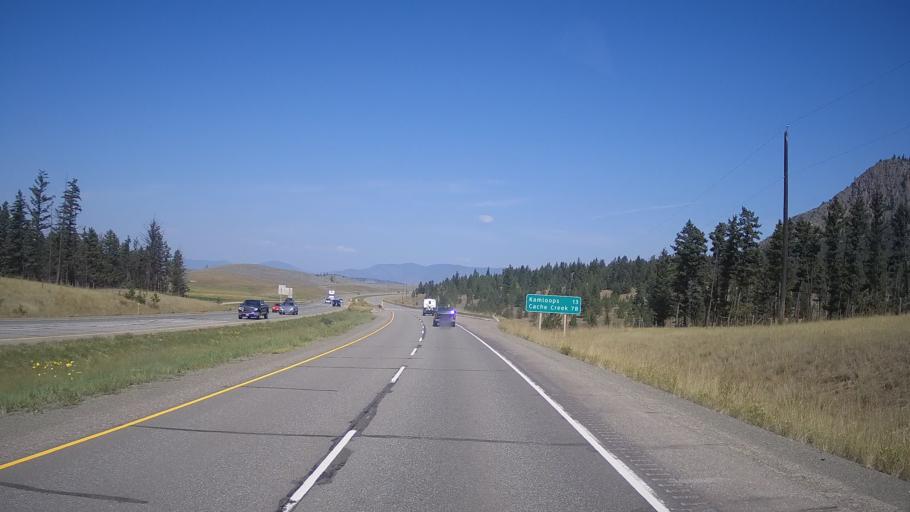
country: CA
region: British Columbia
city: Kamloops
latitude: 50.6251
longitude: -120.4738
